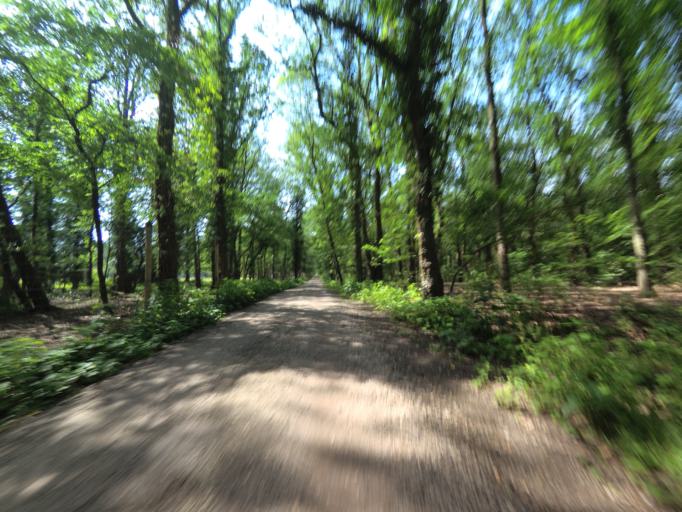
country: NL
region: Gelderland
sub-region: Gemeente Apeldoorn
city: Beekbergen
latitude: 52.1166
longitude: 5.8827
